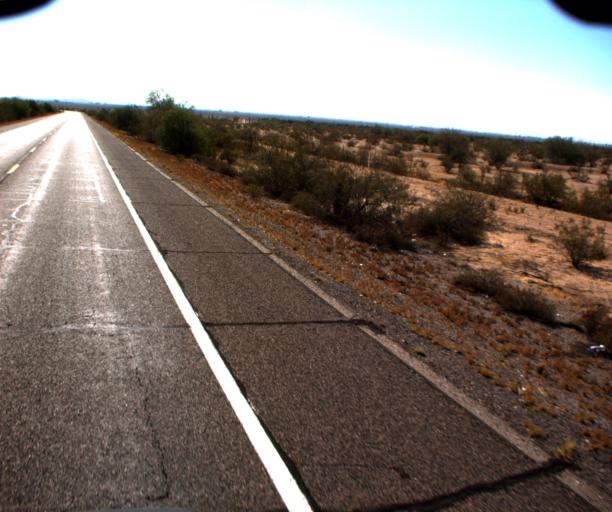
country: US
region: Arizona
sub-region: Pinal County
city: Blackwater
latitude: 33.0187
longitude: -111.6457
